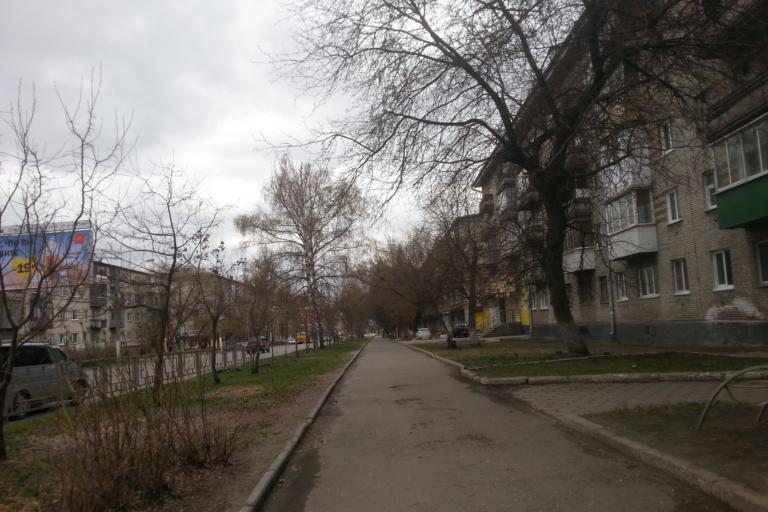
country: RU
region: Altai Krai
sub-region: Gorod Barnaulskiy
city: Barnaul
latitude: 53.3527
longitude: 83.7800
